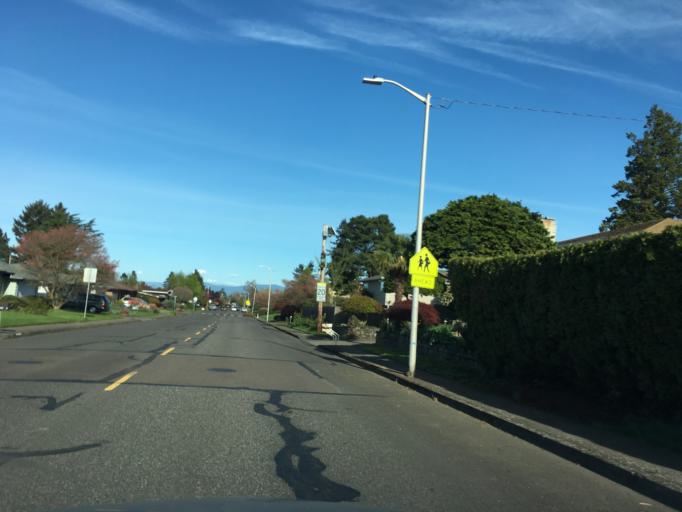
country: US
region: Oregon
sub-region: Multnomah County
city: Lents
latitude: 45.5481
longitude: -122.5290
